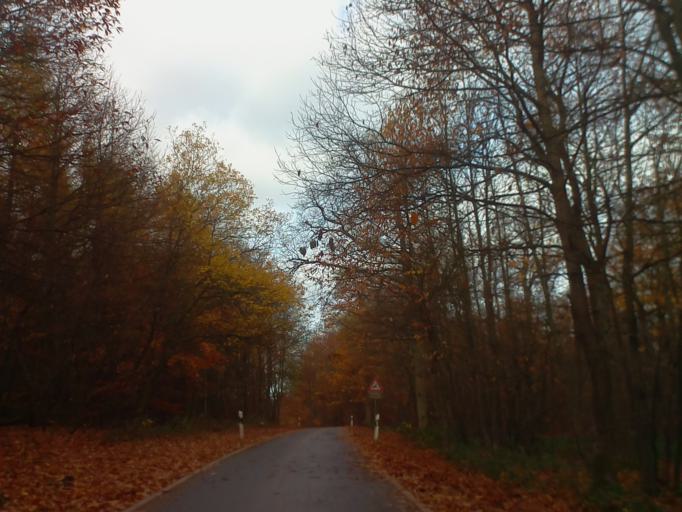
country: DE
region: Rheinland-Pfalz
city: Altleiningen
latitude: 49.4795
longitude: 8.1156
